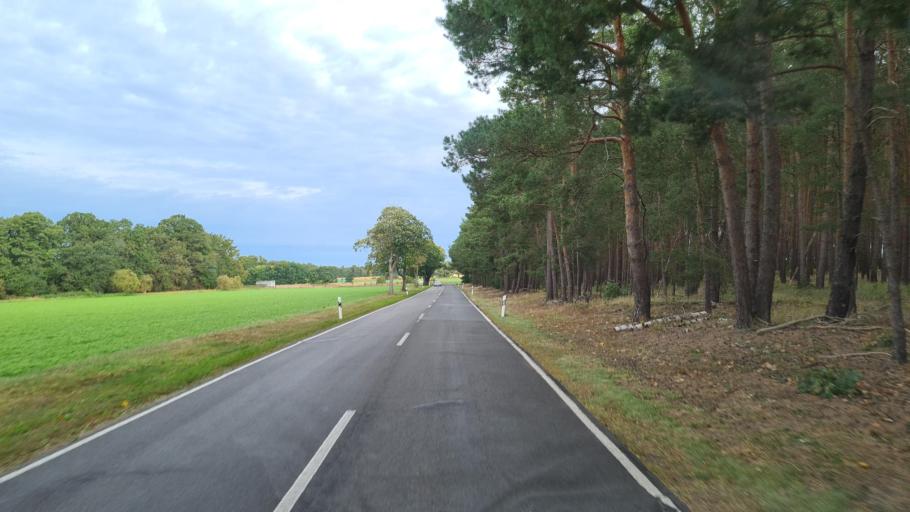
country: DE
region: Brandenburg
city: Kasel-Golzig
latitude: 51.9220
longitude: 13.7105
